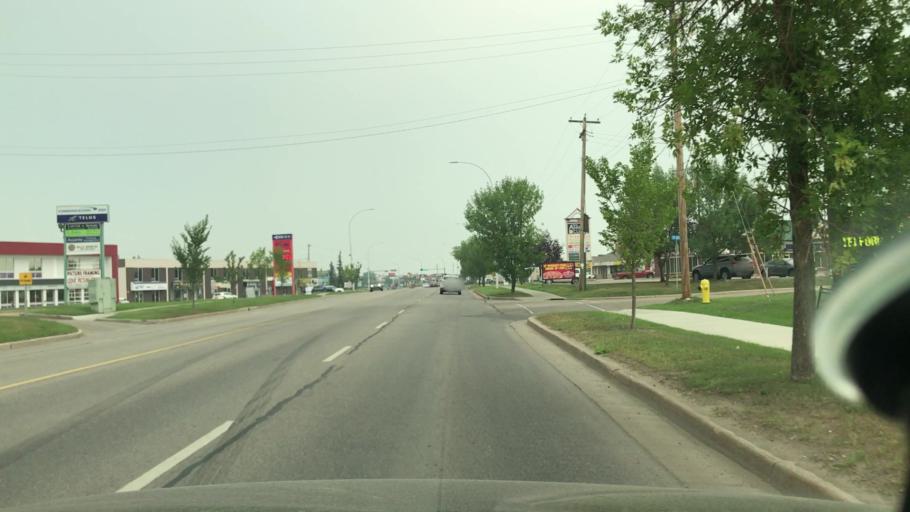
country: CA
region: Alberta
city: Leduc
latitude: 53.2721
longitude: -113.5507
